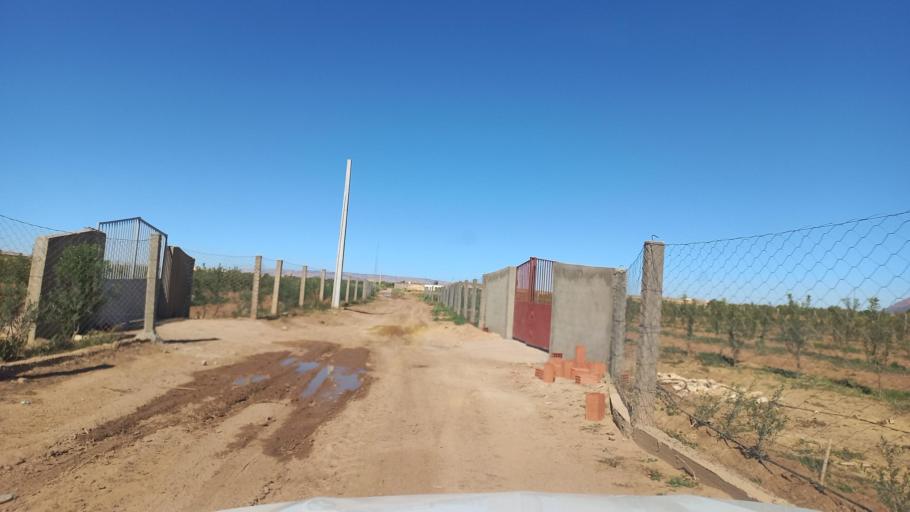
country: TN
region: Al Qasrayn
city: Sbiba
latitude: 35.3923
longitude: 9.0825
